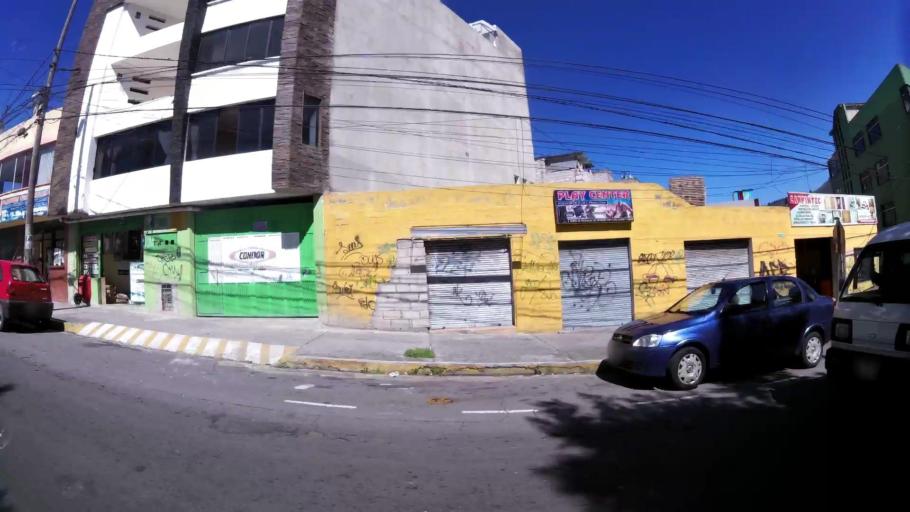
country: EC
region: Pichincha
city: Quito
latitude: -0.2552
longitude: -78.5304
